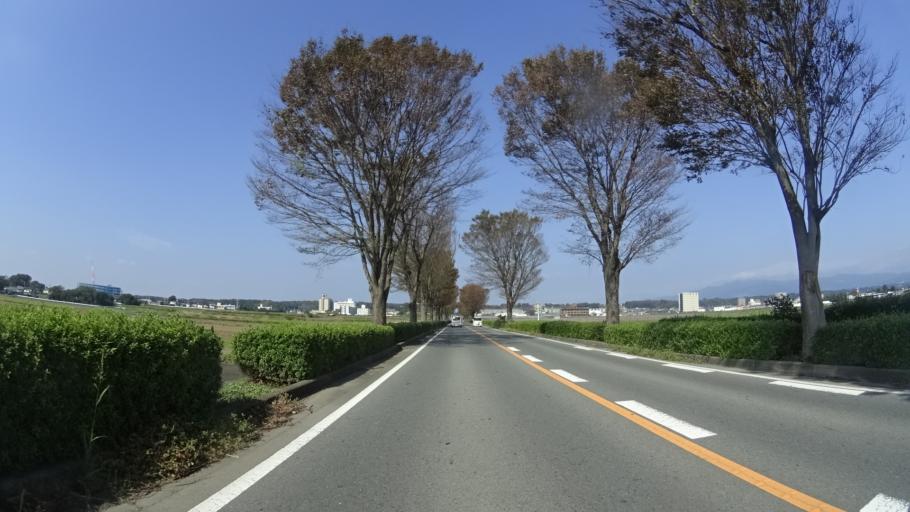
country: JP
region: Kumamoto
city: Ozu
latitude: 32.8690
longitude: 130.8553
